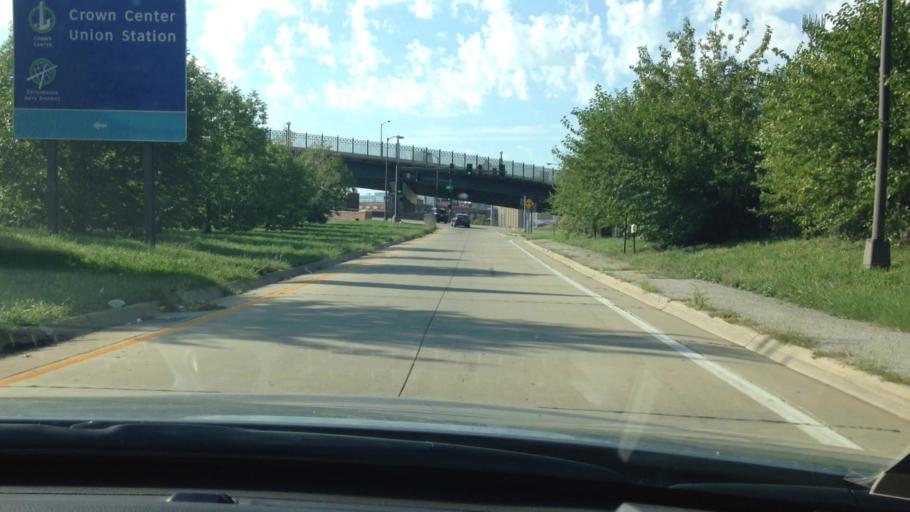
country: US
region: Missouri
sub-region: Jackson County
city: Kansas City
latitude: 39.0854
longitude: -94.5690
